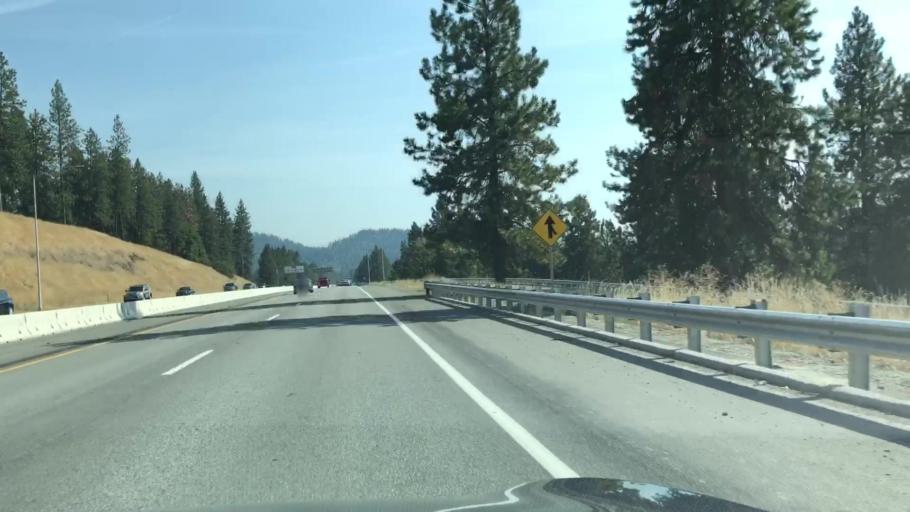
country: US
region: Idaho
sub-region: Kootenai County
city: Coeur d'Alene
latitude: 47.6865
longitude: -116.7628
